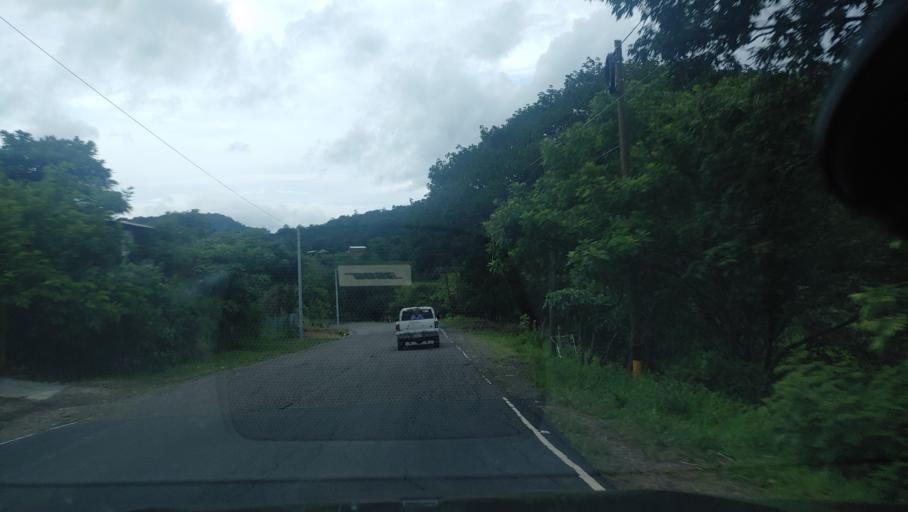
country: HN
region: Choluteca
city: San Marcos de Colon
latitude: 13.3777
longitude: -86.8827
